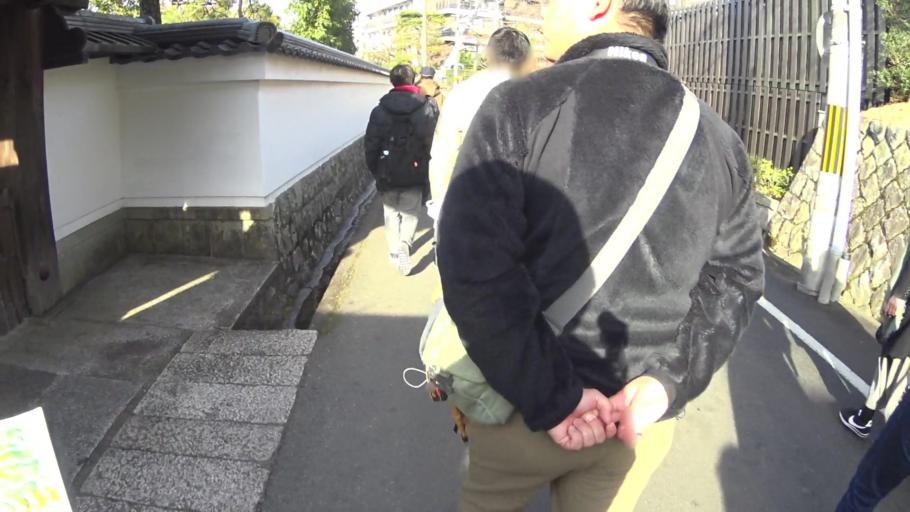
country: JP
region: Kyoto
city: Kyoto
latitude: 35.0125
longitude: 135.7936
